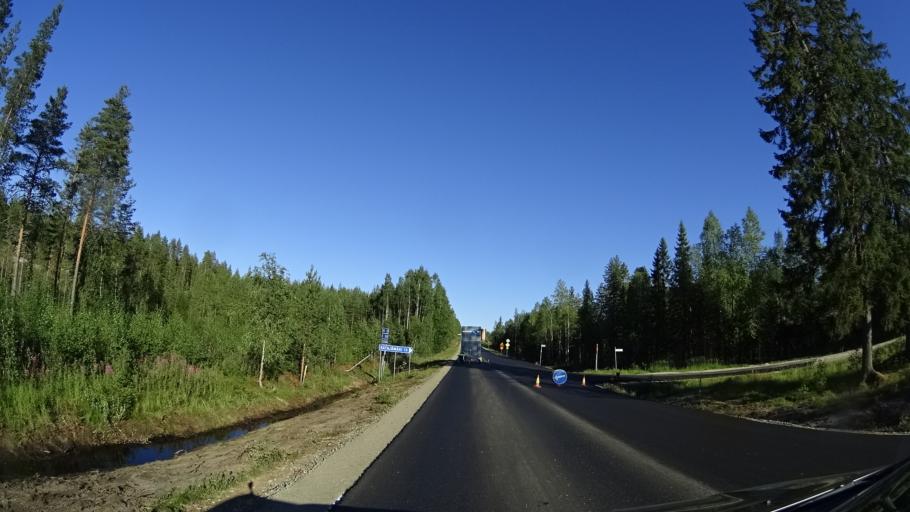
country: FI
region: North Karelia
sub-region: Pielisen Karjala
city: Valtimo
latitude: 63.5584
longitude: 28.6181
